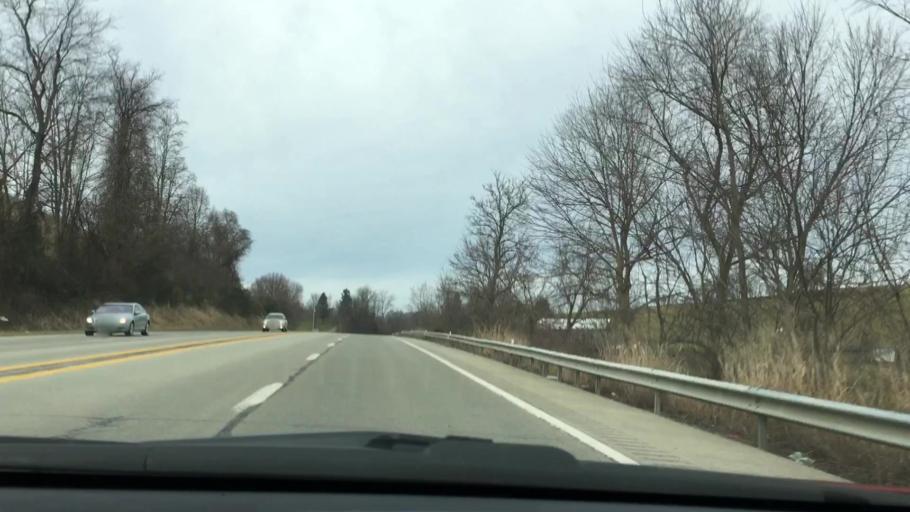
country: US
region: Pennsylvania
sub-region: Fayette County
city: Perryopolis
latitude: 40.0428
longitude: -79.7721
